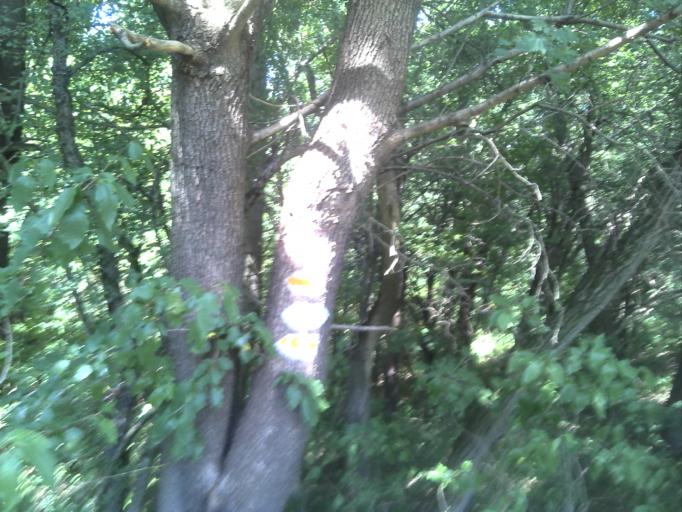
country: HU
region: Pest
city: Pilisszanto
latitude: 47.6428
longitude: 18.8655
